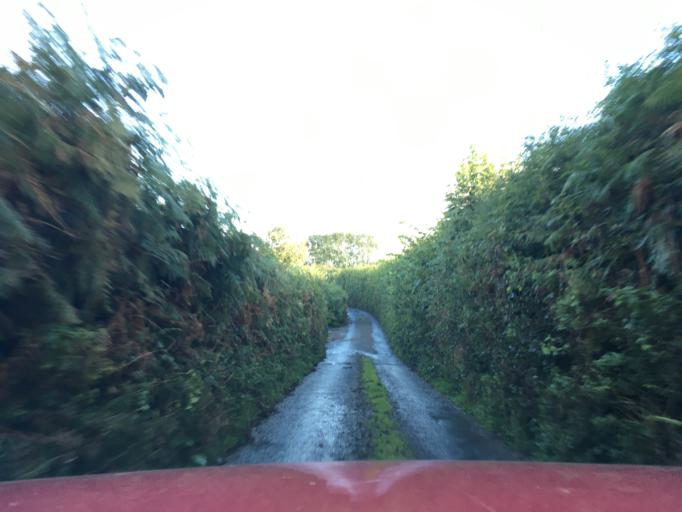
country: GB
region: England
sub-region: Devon
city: Dartmouth
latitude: 50.3406
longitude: -3.6068
